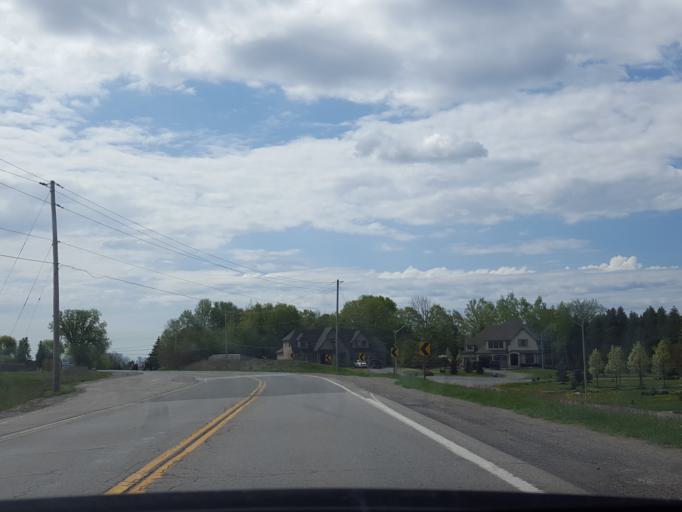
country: CA
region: Ontario
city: Oshawa
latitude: 43.9341
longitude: -78.7124
